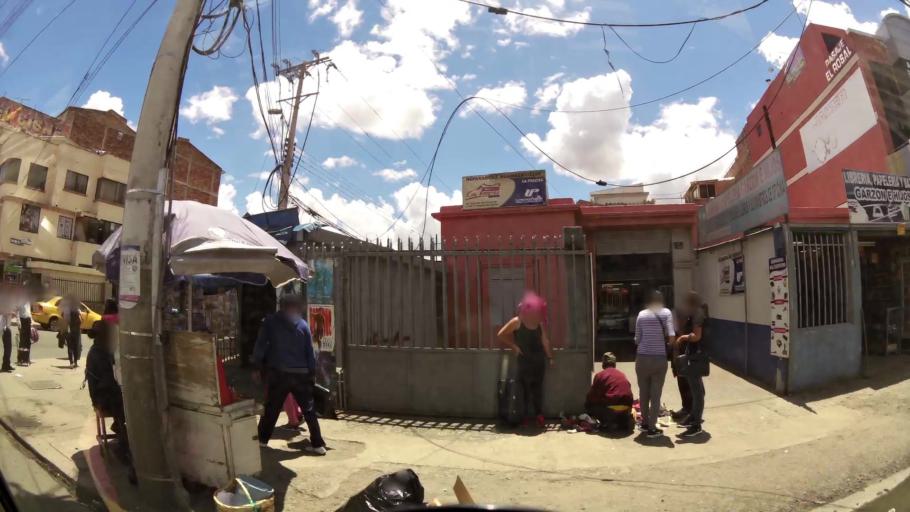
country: EC
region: Azuay
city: Cuenca
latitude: -2.8983
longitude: -79.0262
